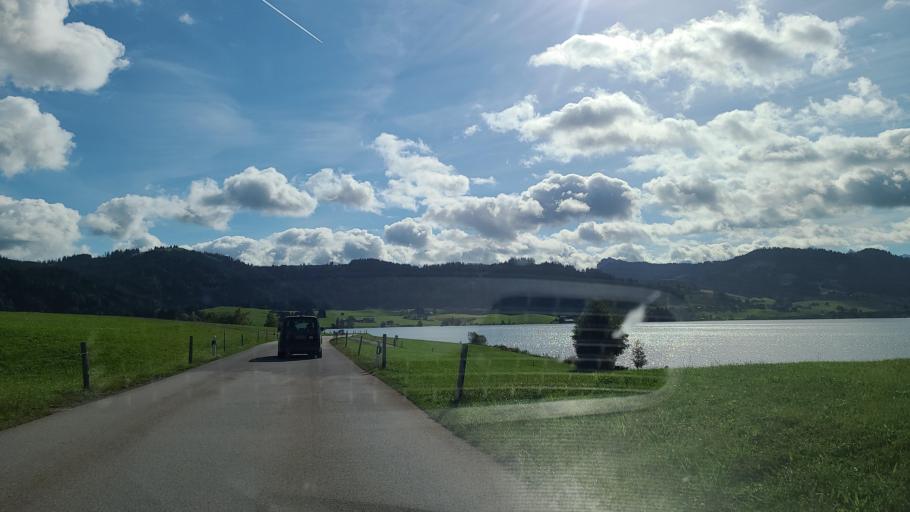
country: CH
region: Schwyz
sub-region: Bezirk Einsiedeln
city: Einsiedeln
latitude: 47.1507
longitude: 8.7720
